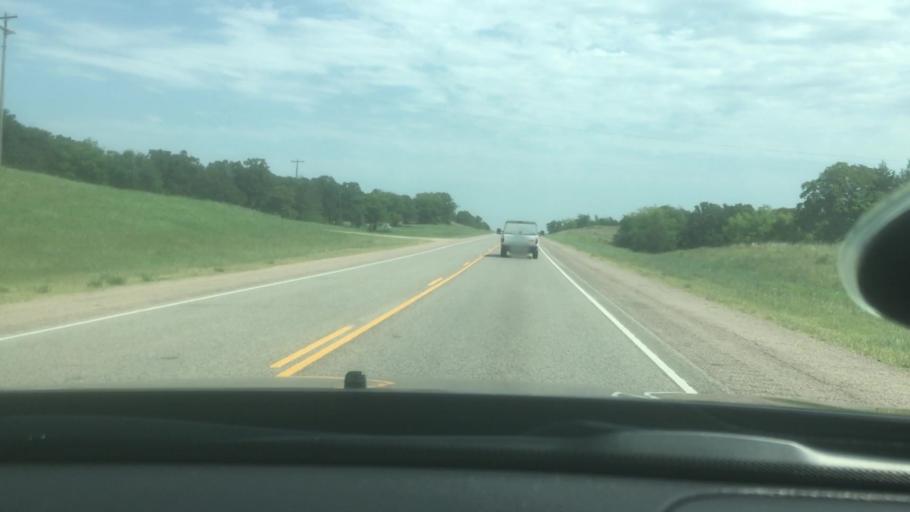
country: US
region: Oklahoma
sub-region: Seminole County
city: Maud
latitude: 35.0519
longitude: -96.9315
